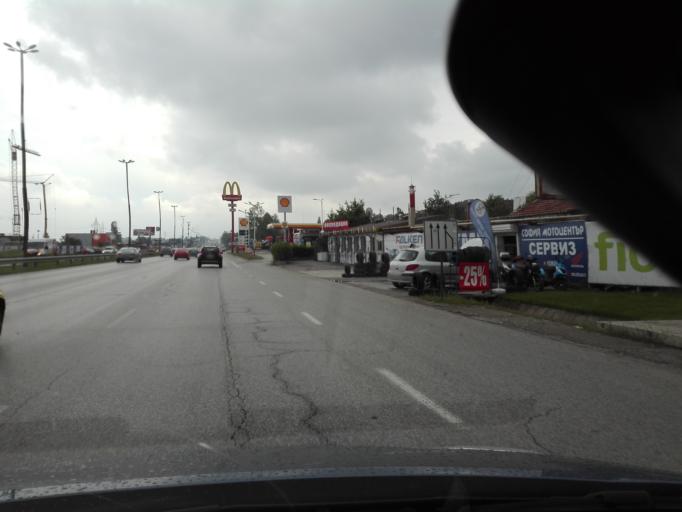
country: BG
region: Sofia-Capital
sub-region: Stolichna Obshtina
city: Sofia
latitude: 42.6512
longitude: 23.2888
